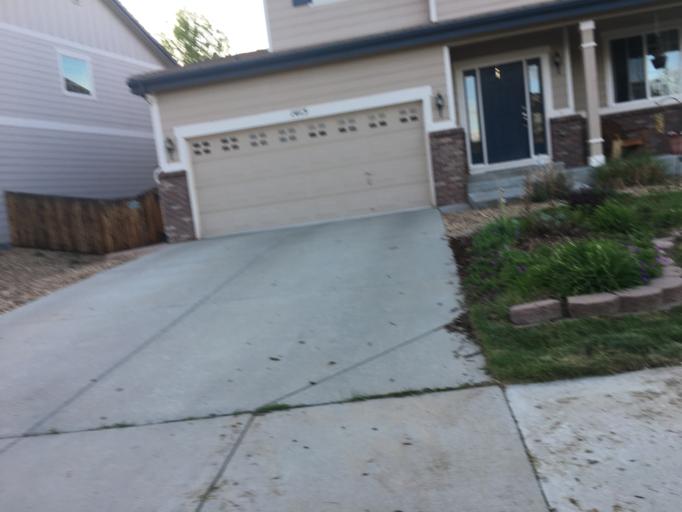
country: US
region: Colorado
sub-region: Boulder County
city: Erie
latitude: 40.0300
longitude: -105.0628
